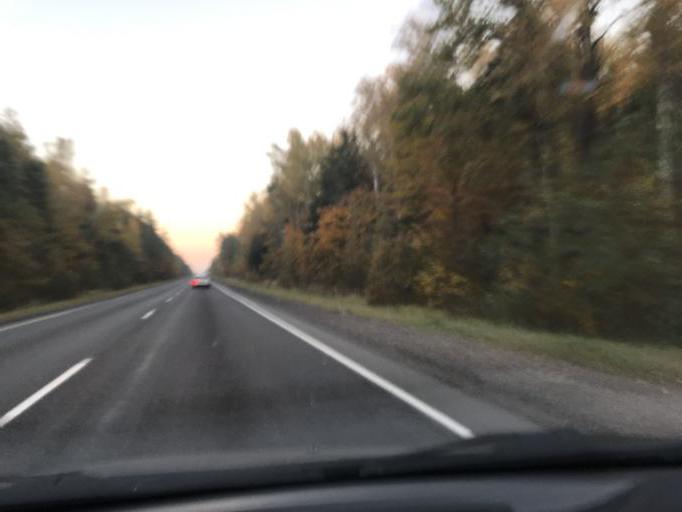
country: BY
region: Mogilev
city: Babruysk
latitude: 53.1525
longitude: 29.0474
